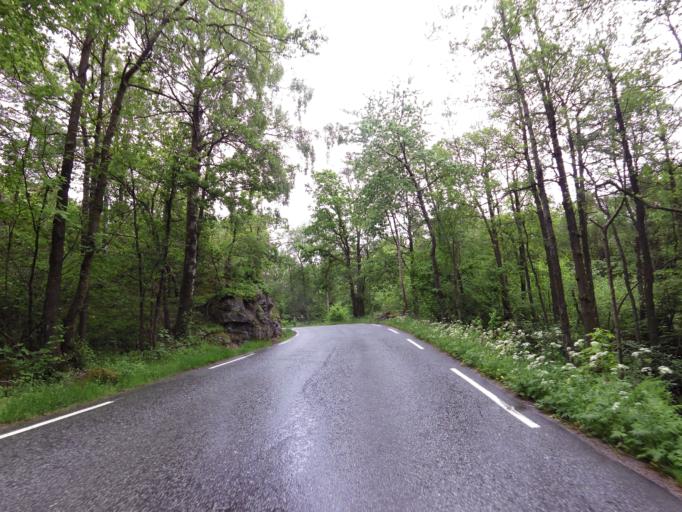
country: NO
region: Vest-Agder
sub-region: Mandal
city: Mandal
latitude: 58.0152
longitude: 7.5116
